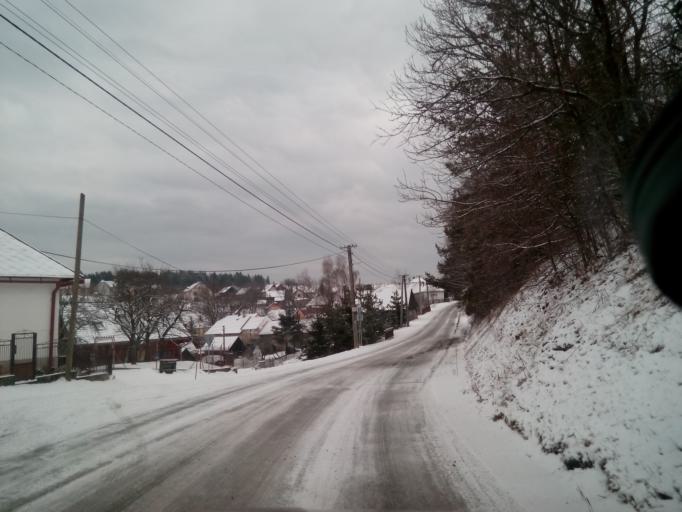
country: SK
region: Presovsky
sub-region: Okres Presov
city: Levoca
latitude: 49.0442
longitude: 20.6422
